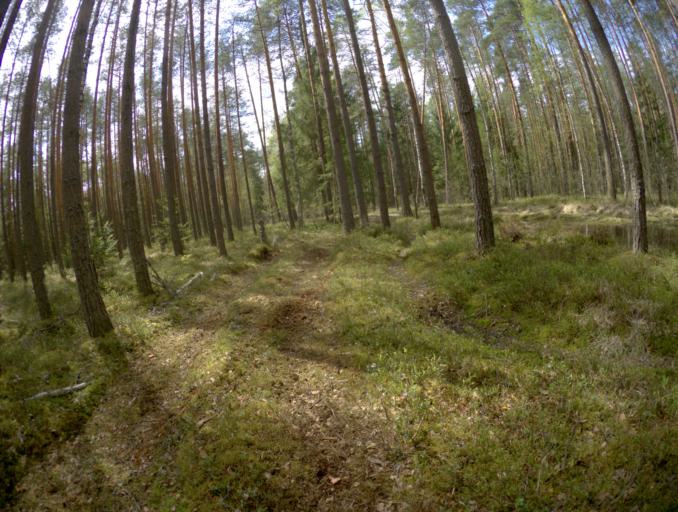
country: RU
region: Vladimir
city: Golovino
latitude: 55.9020
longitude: 40.3926
